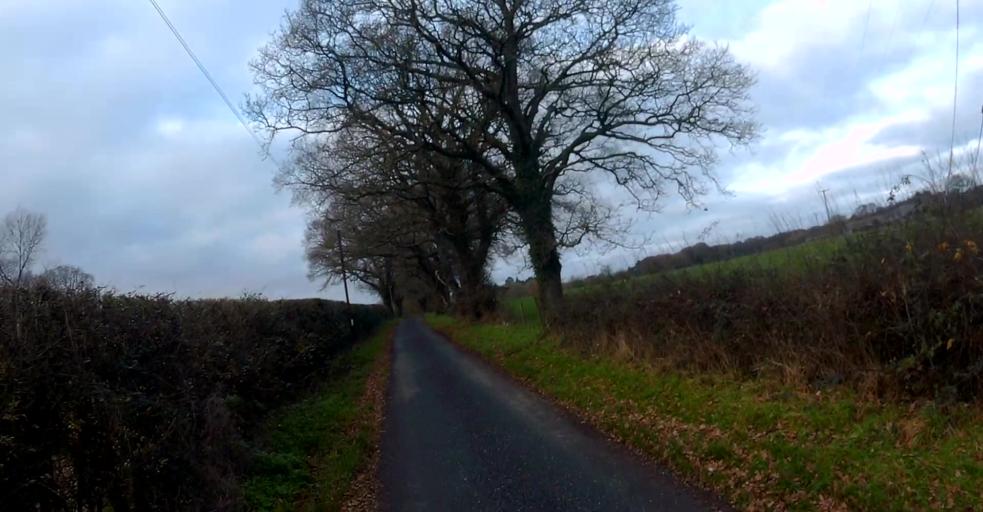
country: GB
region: England
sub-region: Hampshire
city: Basingstoke
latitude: 51.1792
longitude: -1.0986
